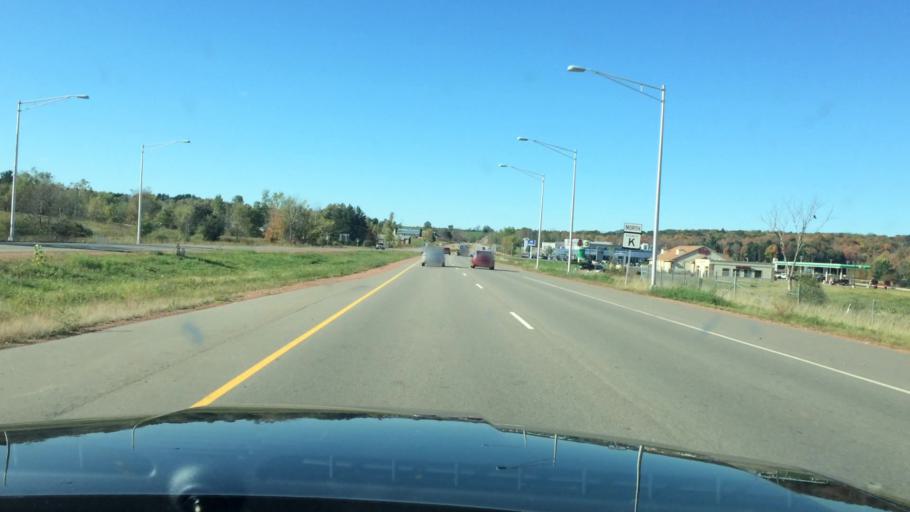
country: US
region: Wisconsin
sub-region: Marathon County
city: Wausau
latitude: 44.9930
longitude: -89.6601
